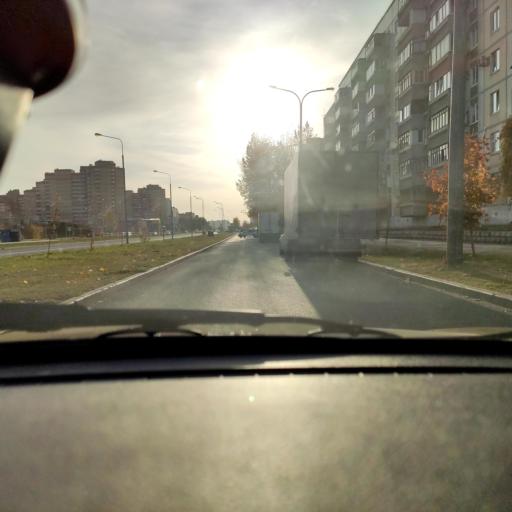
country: RU
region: Samara
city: Tol'yatti
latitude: 53.5425
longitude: 49.3659
